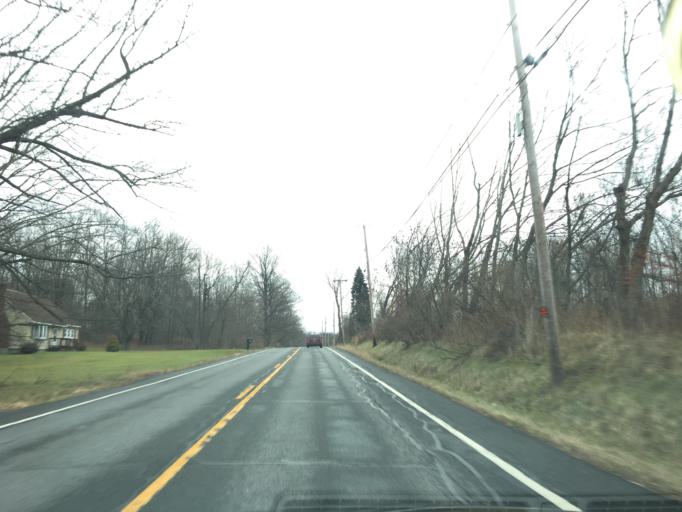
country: US
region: New York
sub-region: Rensselaer County
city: Poestenkill
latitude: 42.6741
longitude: -73.5929
